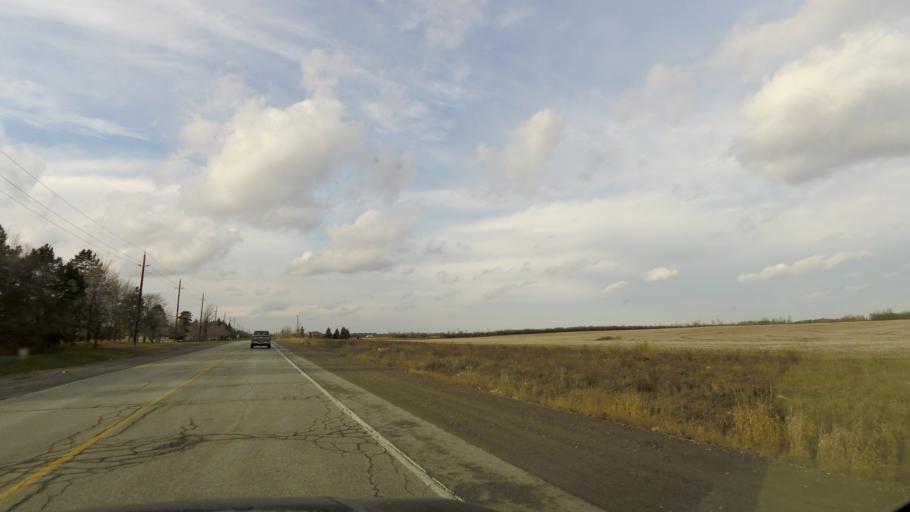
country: CA
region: Ontario
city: Brampton
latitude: 43.8007
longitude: -79.7018
